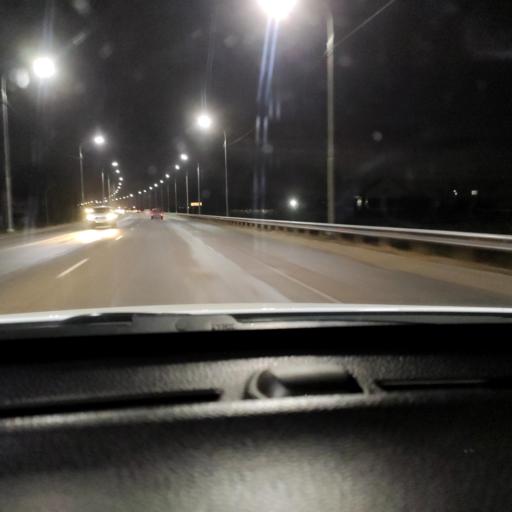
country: RU
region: Voronezj
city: Somovo
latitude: 51.6890
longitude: 39.3595
